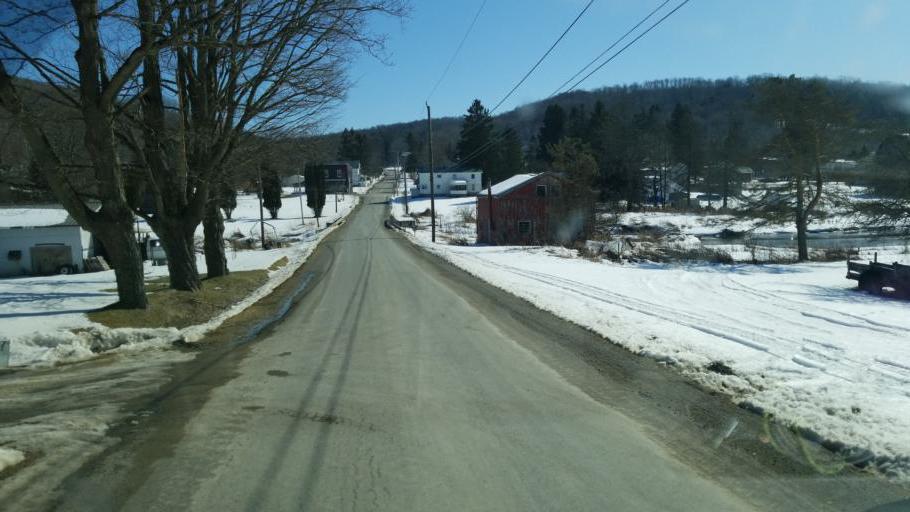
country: US
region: New York
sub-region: Allegany County
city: Andover
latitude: 42.0854
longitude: -77.6640
